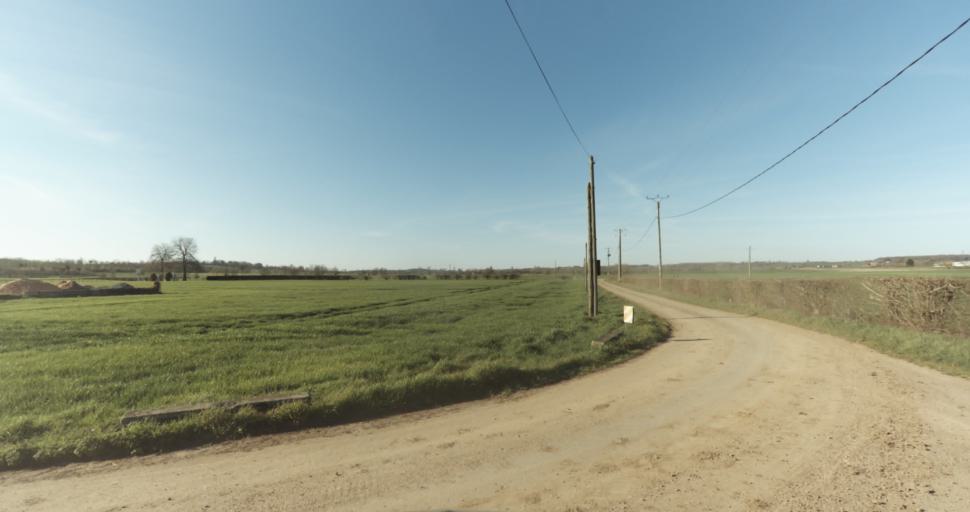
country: FR
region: Lower Normandy
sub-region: Departement du Calvados
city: Saint-Pierre-sur-Dives
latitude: 49.0159
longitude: 0.0236
